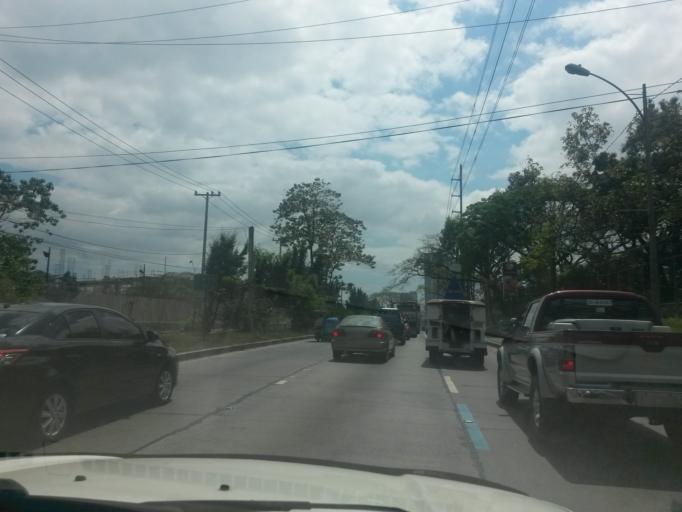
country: PH
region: Metro Manila
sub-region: Quezon City
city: Quezon City
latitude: 14.6521
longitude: 121.0743
